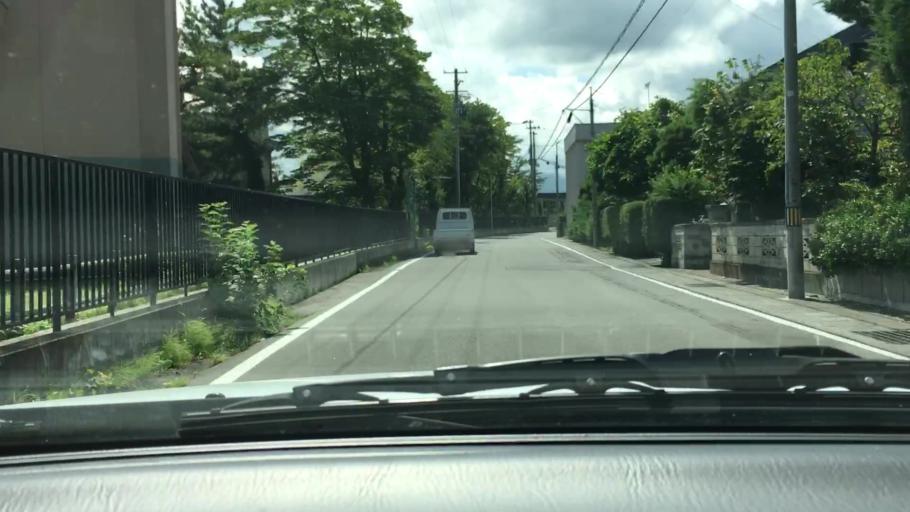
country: JP
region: Aomori
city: Hirosaki
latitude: 40.5892
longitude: 140.4706
